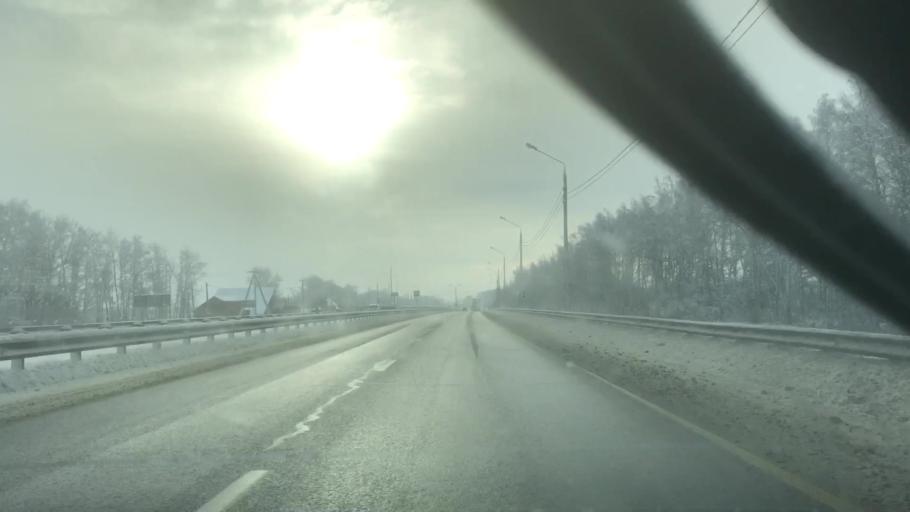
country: RU
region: Tula
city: Venev
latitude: 54.3464
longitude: 38.1542
